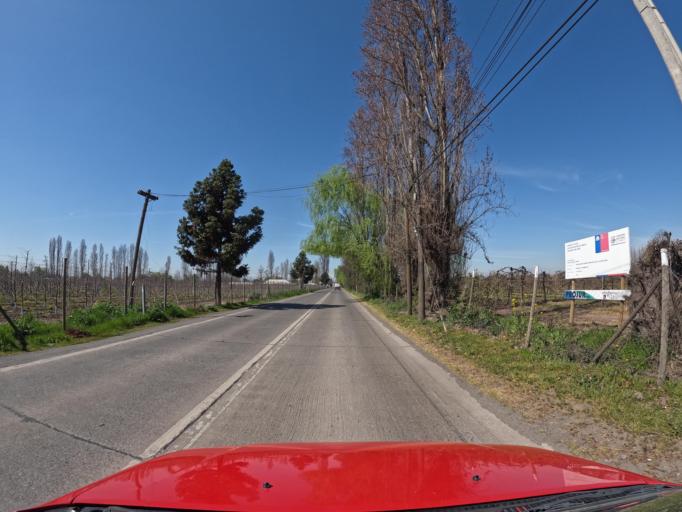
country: CL
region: Maule
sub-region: Provincia de Curico
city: Rauco
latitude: -35.0026
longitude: -71.3291
